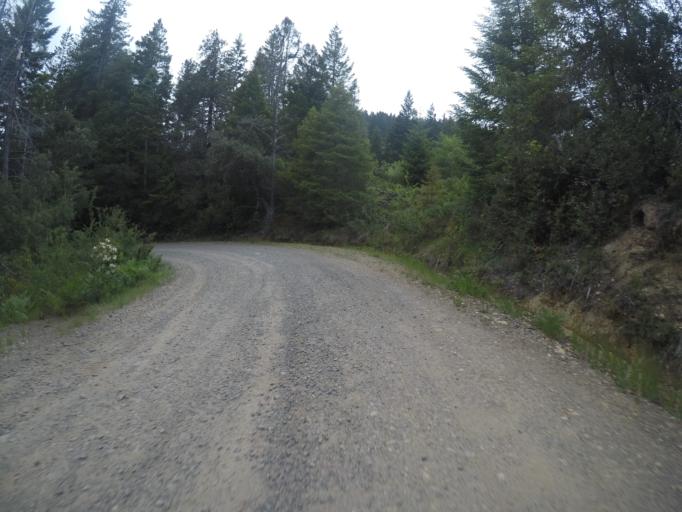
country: US
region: California
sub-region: Del Norte County
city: Bertsch-Oceanview
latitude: 41.7417
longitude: -123.8762
